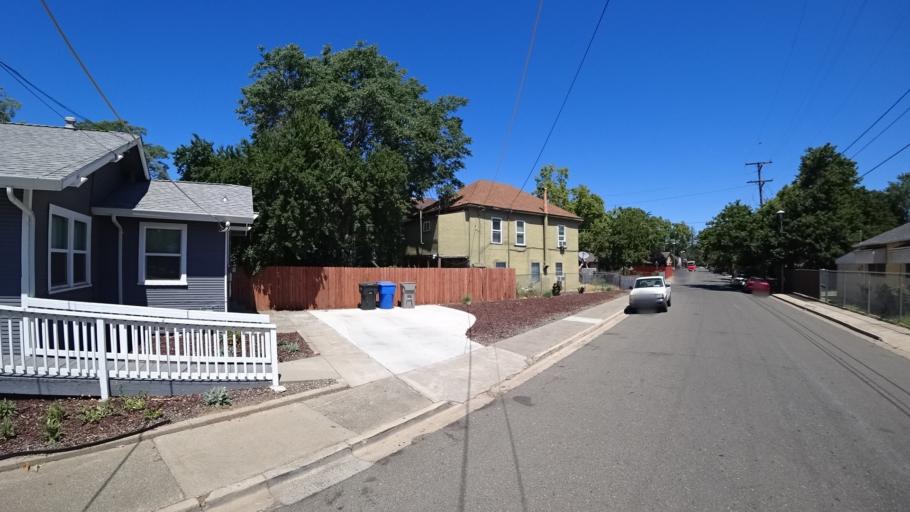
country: US
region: California
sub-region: Sacramento County
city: Sacramento
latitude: 38.5491
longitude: -121.4602
